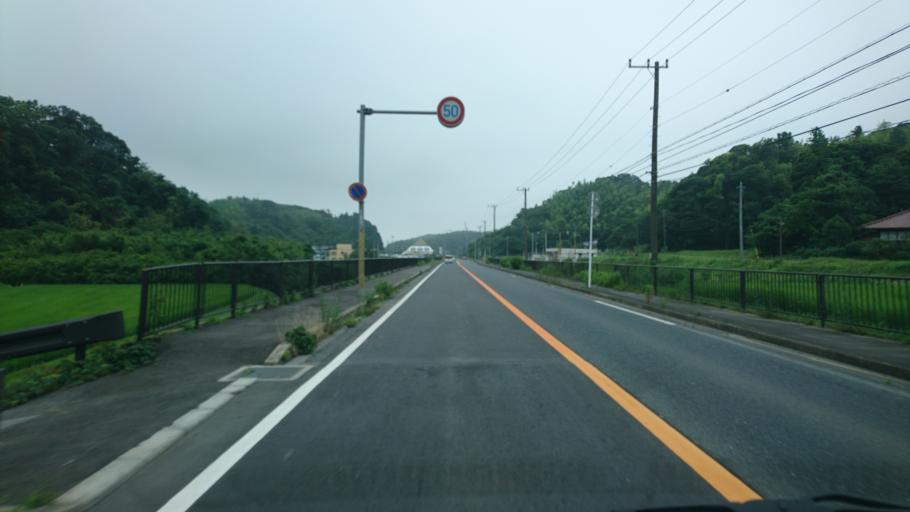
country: JP
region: Chiba
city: Kimitsu
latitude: 35.2745
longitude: 139.9030
